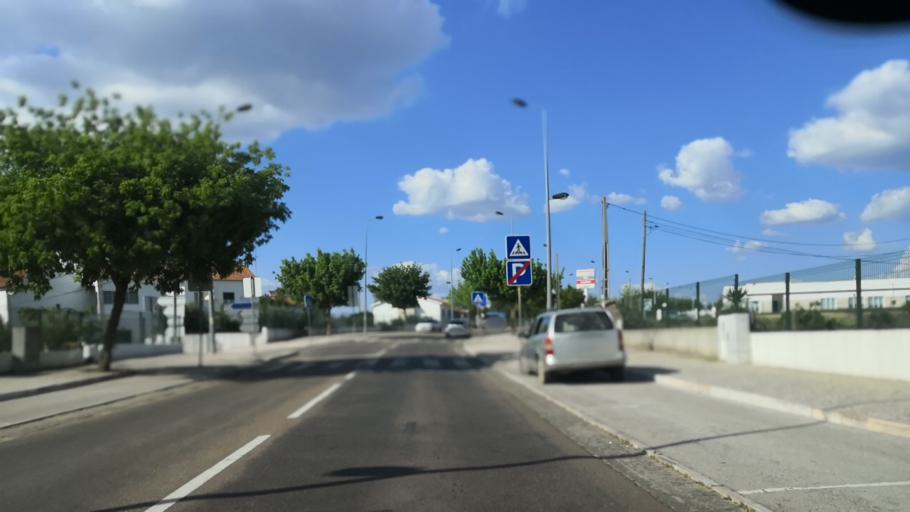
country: PT
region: Evora
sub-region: Estremoz
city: Estremoz
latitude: 38.8520
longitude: -7.5839
